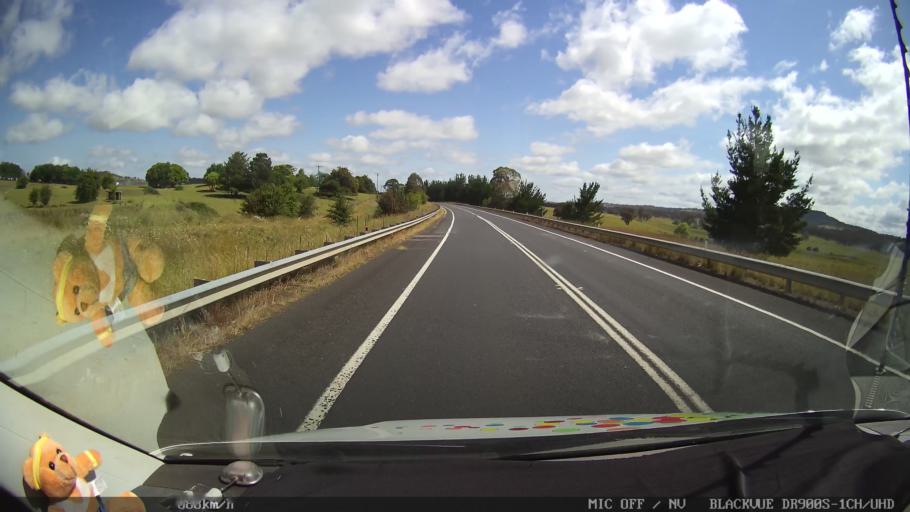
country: AU
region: New South Wales
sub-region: Glen Innes Severn
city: Glen Innes
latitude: -29.8850
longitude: 151.7341
